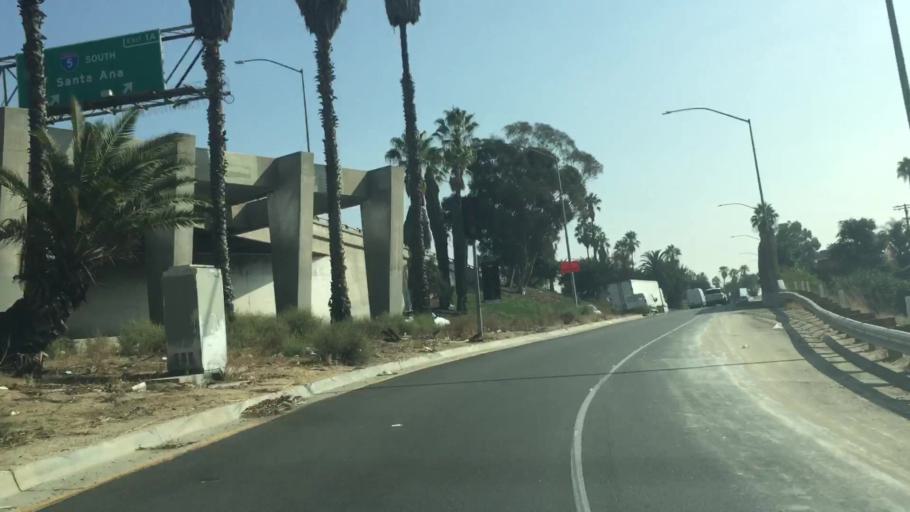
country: US
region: California
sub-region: Los Angeles County
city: Boyle Heights
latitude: 34.0288
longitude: -118.2174
